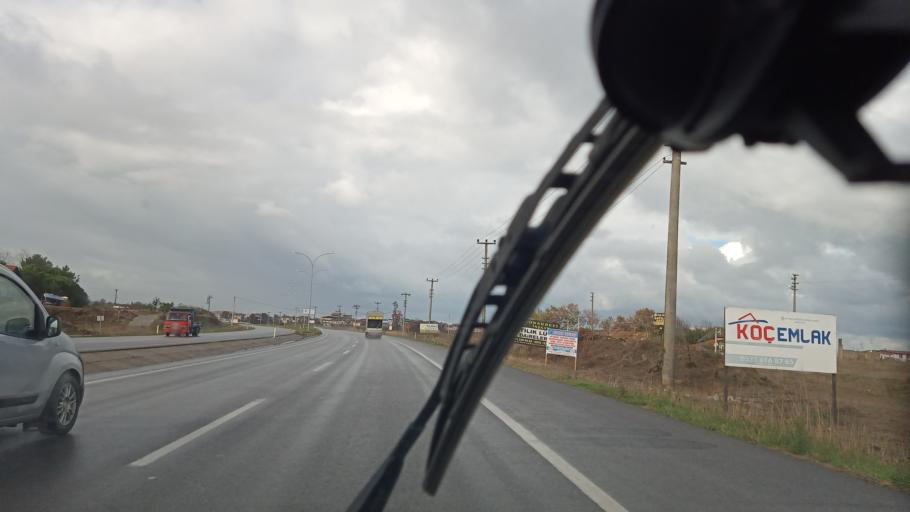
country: TR
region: Sakarya
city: Karasu
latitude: 41.0866
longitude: 30.7517
